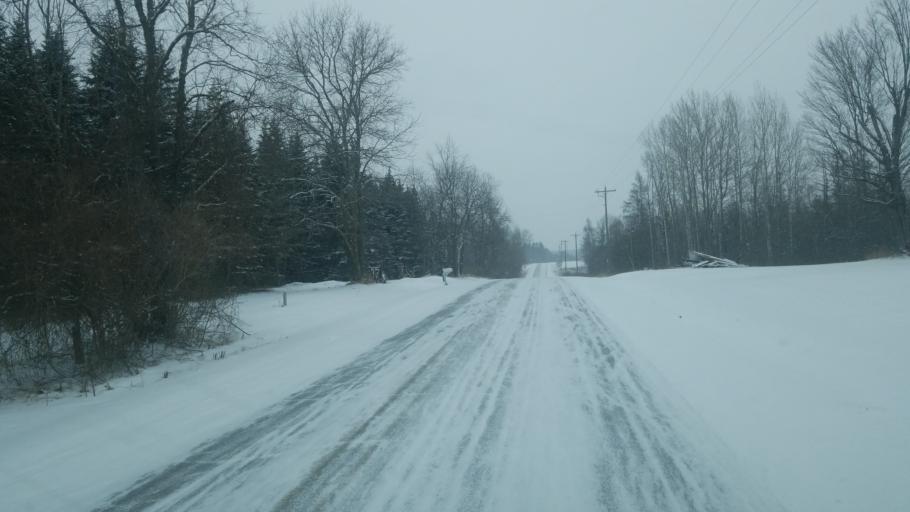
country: US
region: Michigan
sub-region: Osceola County
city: Reed City
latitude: 43.8081
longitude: -85.4023
